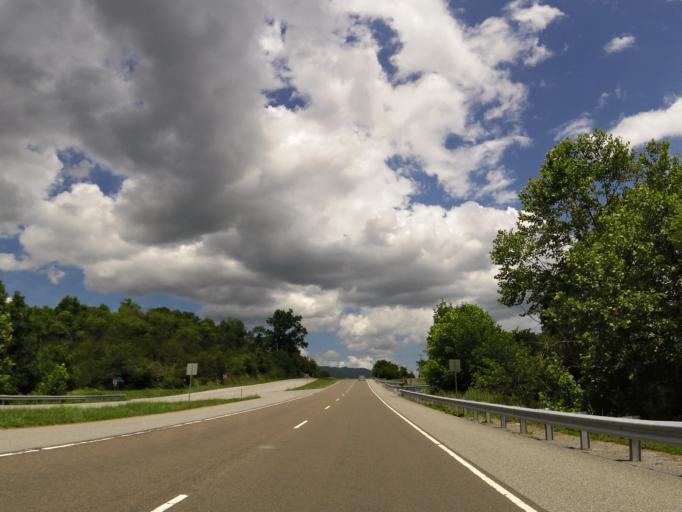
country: US
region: Tennessee
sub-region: Claiborne County
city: Harrogate
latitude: 36.6214
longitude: -83.5481
